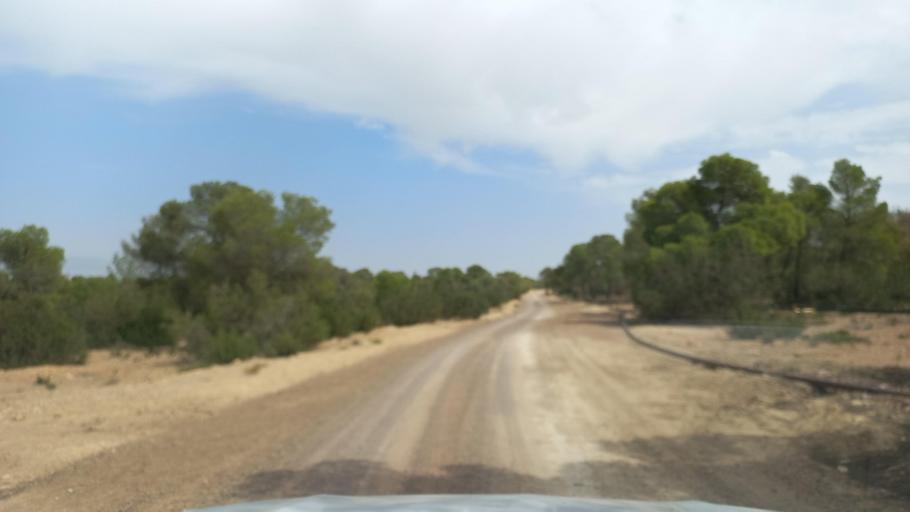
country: TN
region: Al Qasrayn
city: Kasserine
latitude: 35.3825
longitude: 8.8844
